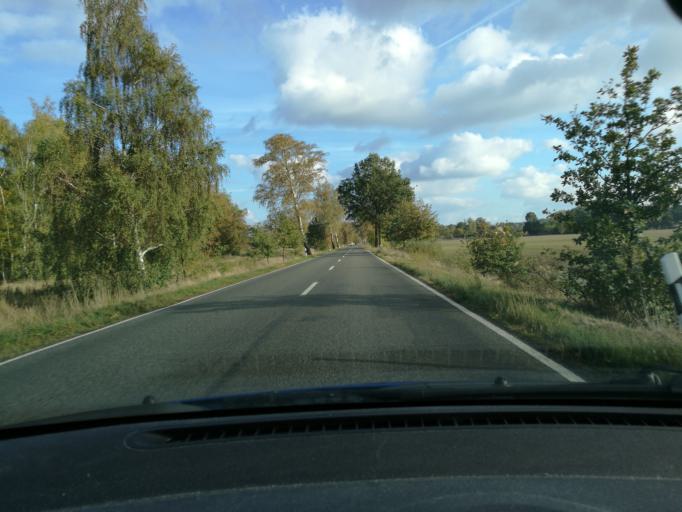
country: DE
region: Saxony-Anhalt
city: Luftkurort Arendsee
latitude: 52.8977
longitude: 11.4356
